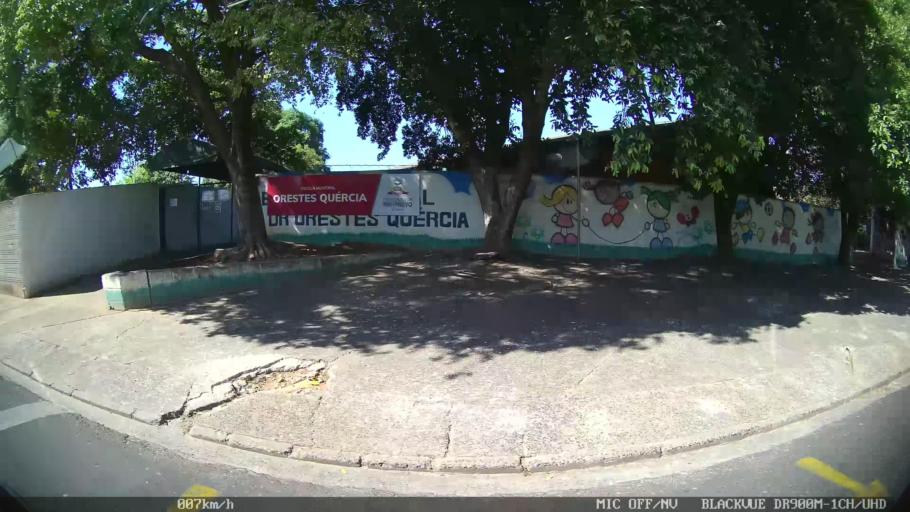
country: BR
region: Sao Paulo
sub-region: Sao Jose Do Rio Preto
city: Sao Jose do Rio Preto
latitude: -20.7744
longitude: -49.4182
